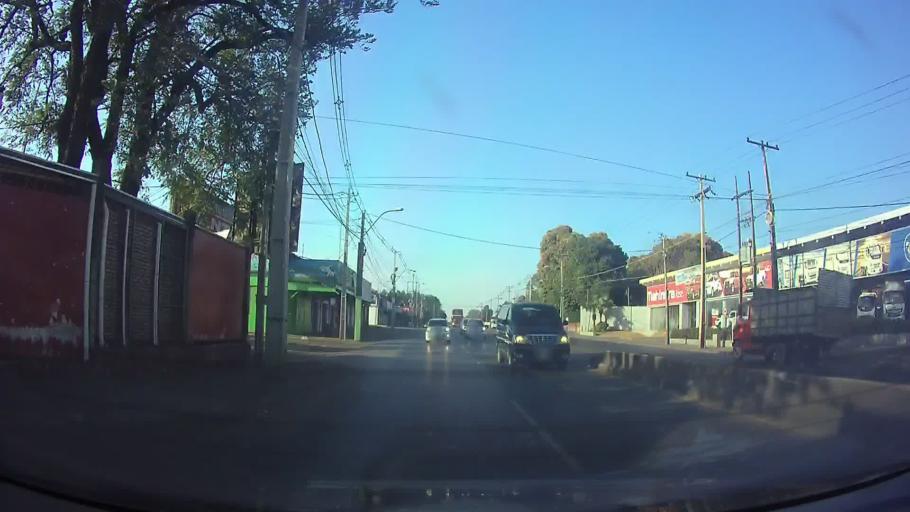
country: PY
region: Central
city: Lambare
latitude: -25.3278
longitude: -57.5702
